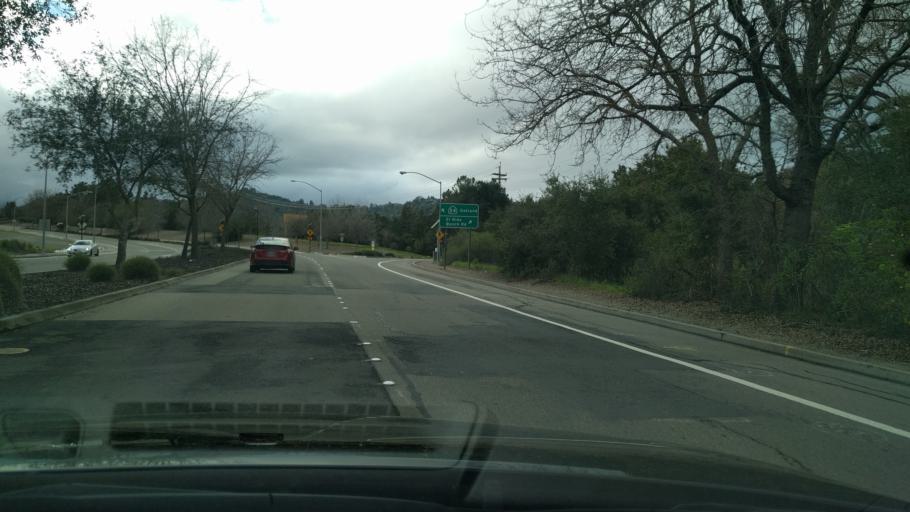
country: US
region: California
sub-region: Contra Costa County
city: Lafayette
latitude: 37.8899
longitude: -122.1433
